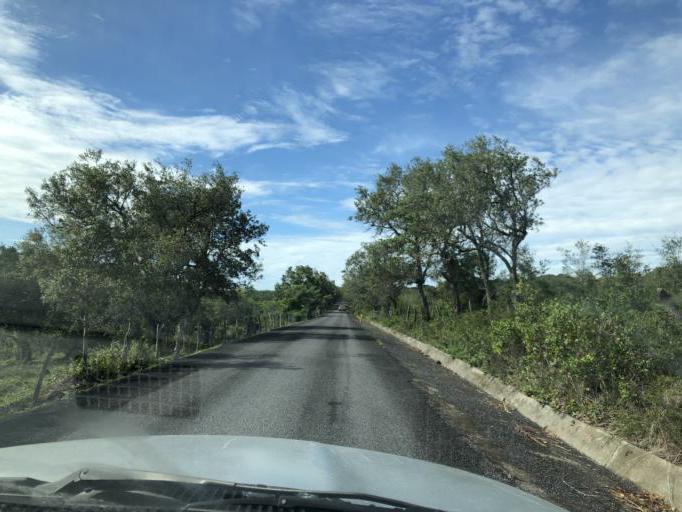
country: MX
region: Veracruz
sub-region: Juchique de Ferrer
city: Plan de las Hayas
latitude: 19.7796
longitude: -96.5566
